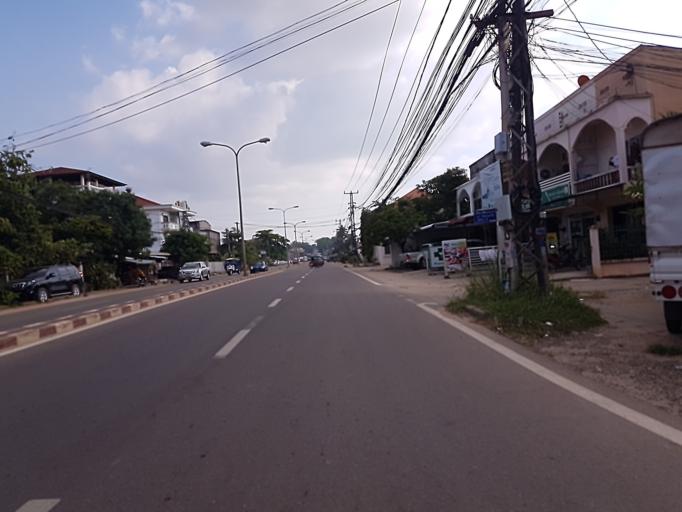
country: TH
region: Nong Khai
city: Si Chiang Mai
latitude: 17.9155
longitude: 102.6198
